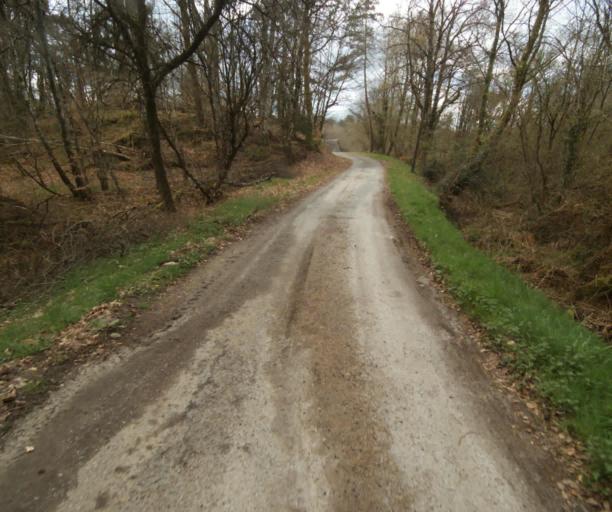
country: FR
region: Limousin
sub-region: Departement de la Correze
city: Correze
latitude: 45.2843
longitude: 1.9029
